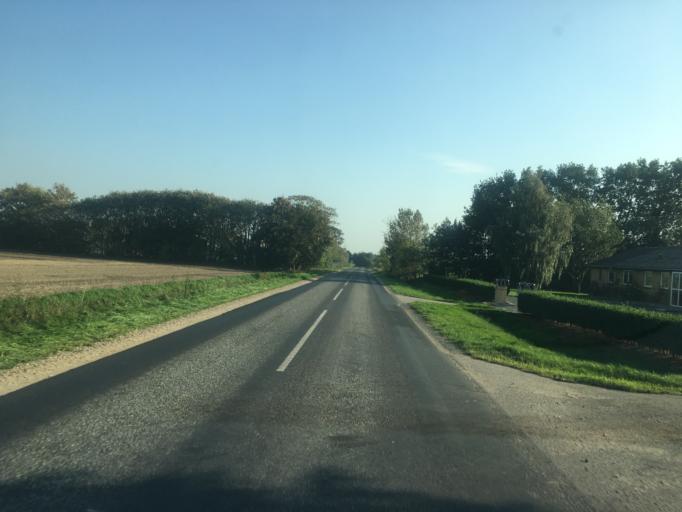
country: DE
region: Schleswig-Holstein
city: Bramstedtlund
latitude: 54.9487
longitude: 9.0595
